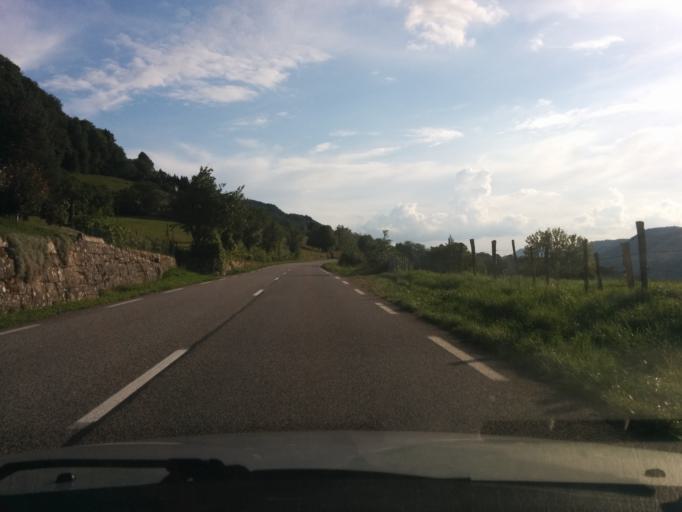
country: FR
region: Rhone-Alpes
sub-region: Departement de la Savoie
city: Saint-Beron
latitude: 45.4931
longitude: 5.7261
